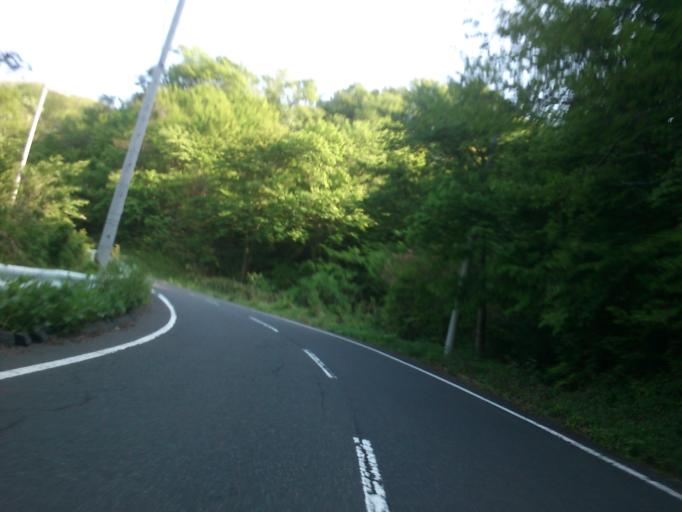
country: JP
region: Kyoto
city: Miyazu
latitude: 35.7270
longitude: 135.1859
